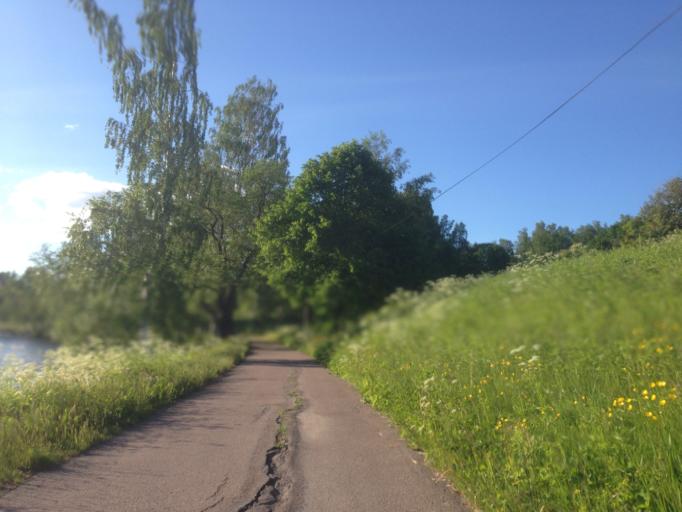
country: SE
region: Dalarna
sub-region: Ludvika Kommun
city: Ludvika
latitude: 60.1035
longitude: 15.2154
